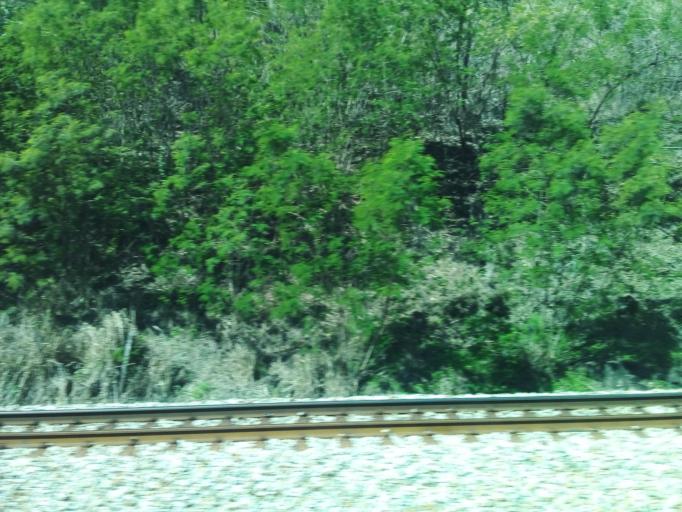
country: BR
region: Minas Gerais
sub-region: Governador Valadares
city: Governador Valadares
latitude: -18.8482
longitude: -41.8617
